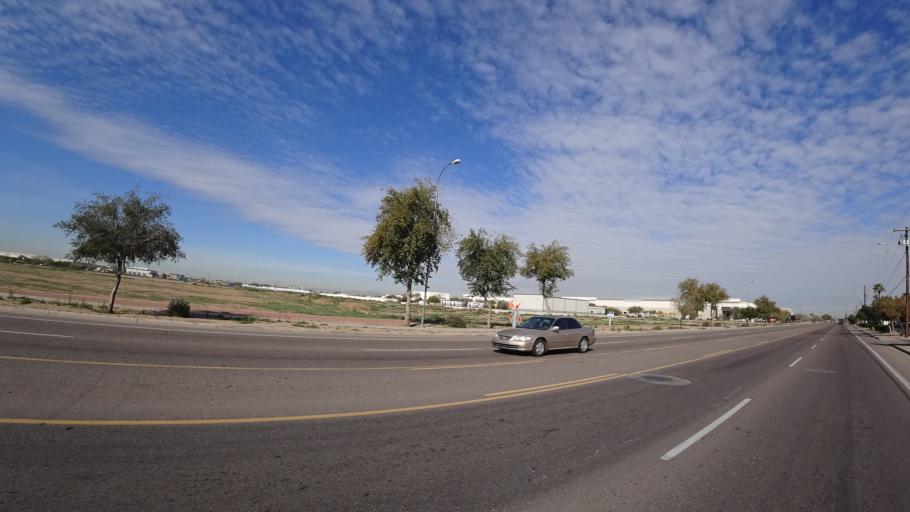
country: US
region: Arizona
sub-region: Maricopa County
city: Laveen
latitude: 33.4239
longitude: -112.1693
